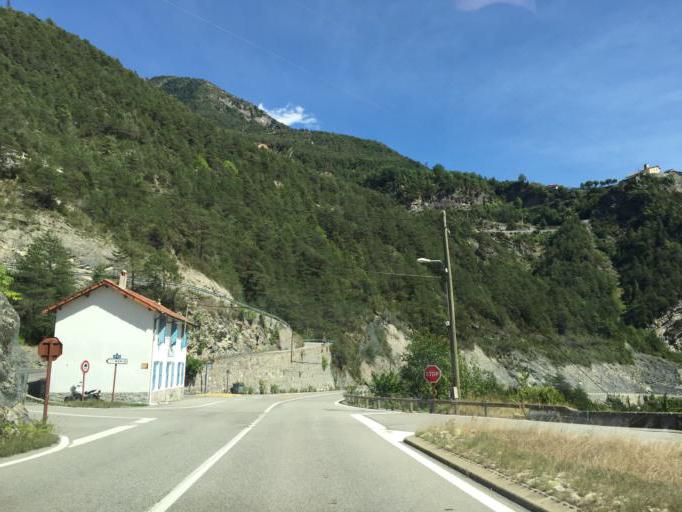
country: FR
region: Provence-Alpes-Cote d'Azur
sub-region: Departement des Alpes-Maritimes
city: Saint-Martin-Vesubie
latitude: 44.0363
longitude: 7.1288
